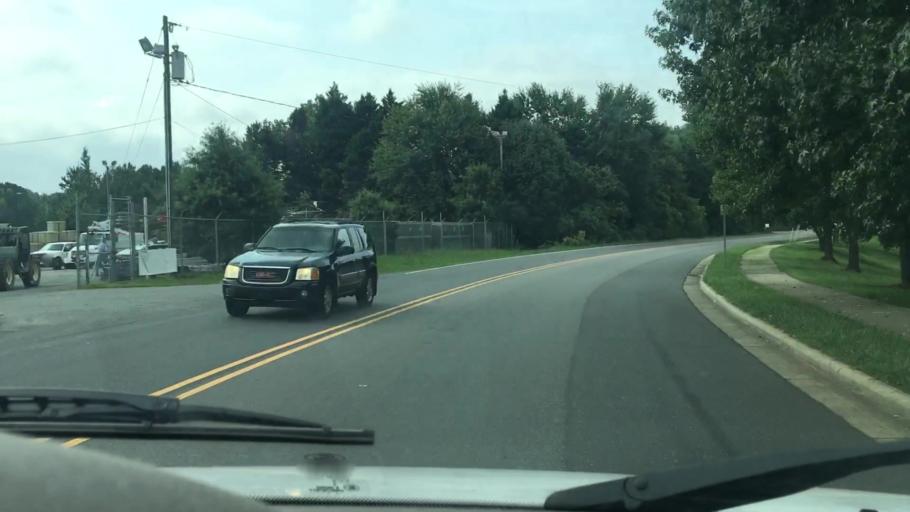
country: US
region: North Carolina
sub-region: Mecklenburg County
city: Charlotte
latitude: 35.3105
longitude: -80.8490
